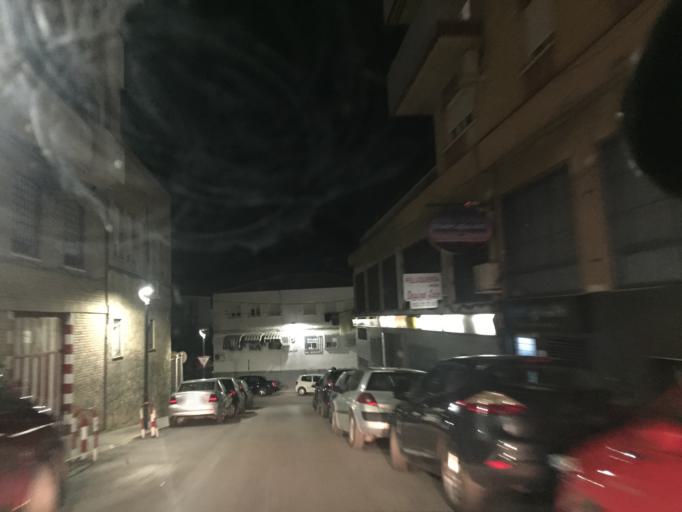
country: ES
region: Andalusia
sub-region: Provincia de Jaen
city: Jaen
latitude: 37.7779
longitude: -3.7968
